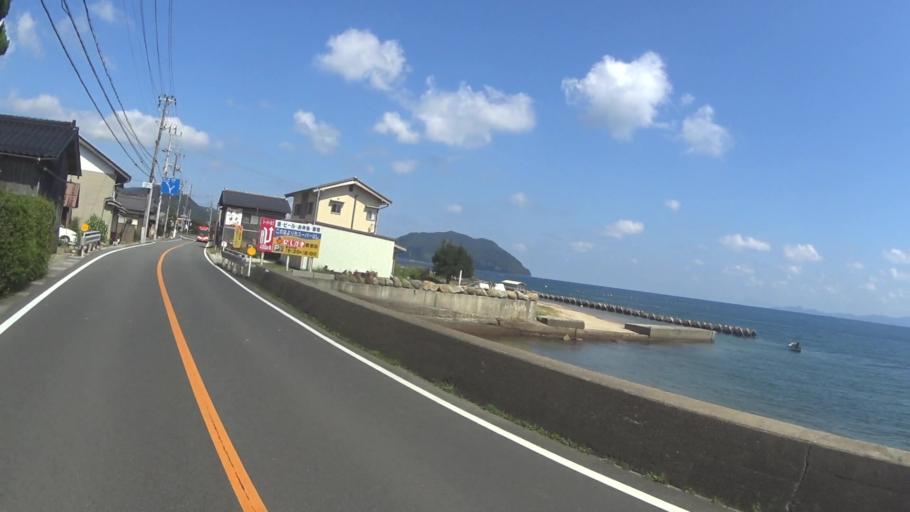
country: JP
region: Kyoto
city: Miyazu
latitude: 35.6548
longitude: 135.2577
